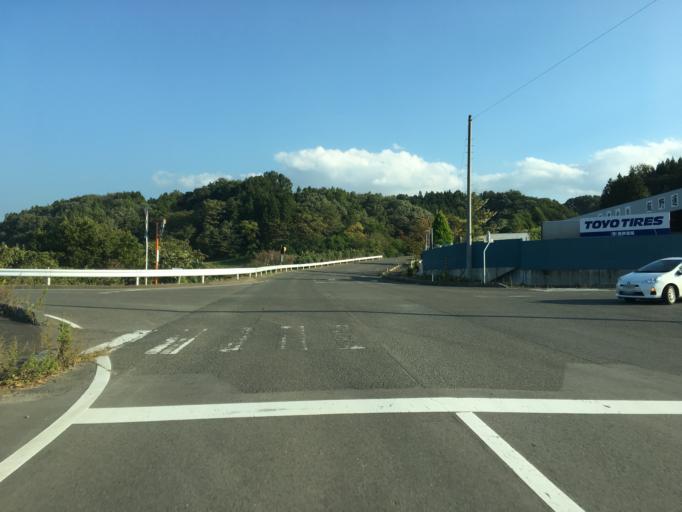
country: JP
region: Fukushima
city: Fukushima-shi
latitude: 37.6561
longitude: 140.5439
